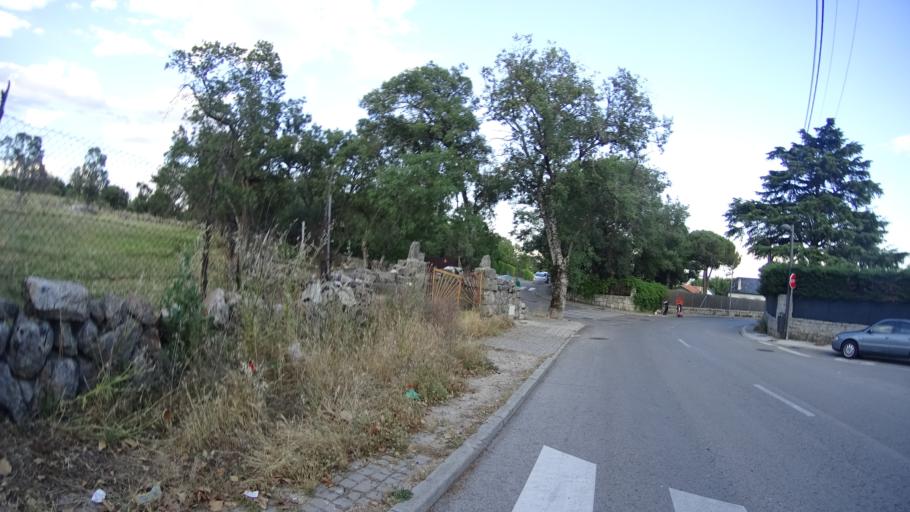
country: ES
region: Madrid
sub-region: Provincia de Madrid
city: Hoyo de Manzanares
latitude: 40.6262
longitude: -3.9071
